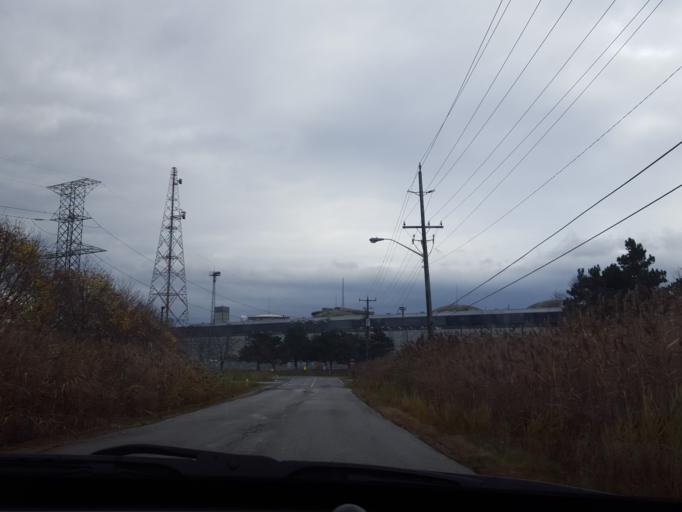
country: CA
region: Ontario
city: Ajax
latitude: 43.8144
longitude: -79.0703
